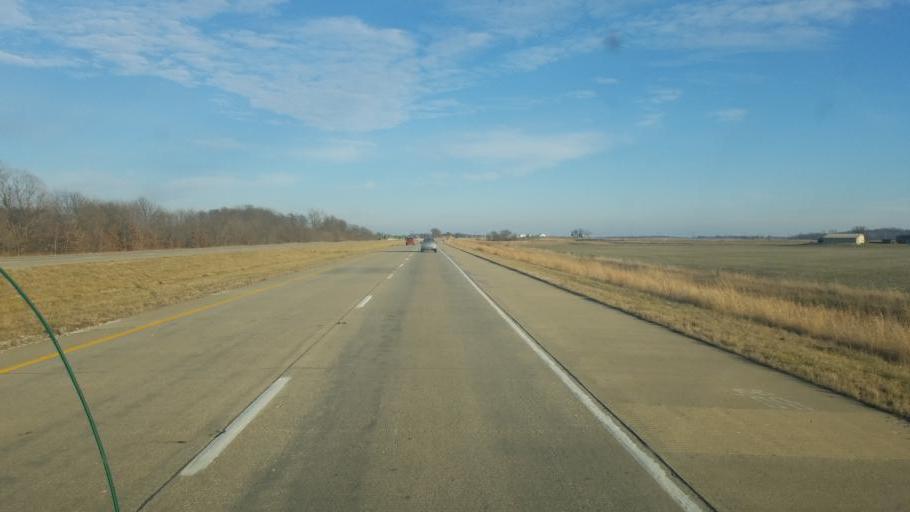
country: US
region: Indiana
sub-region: Knox County
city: Bicknell
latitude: 38.6762
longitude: -87.3777
